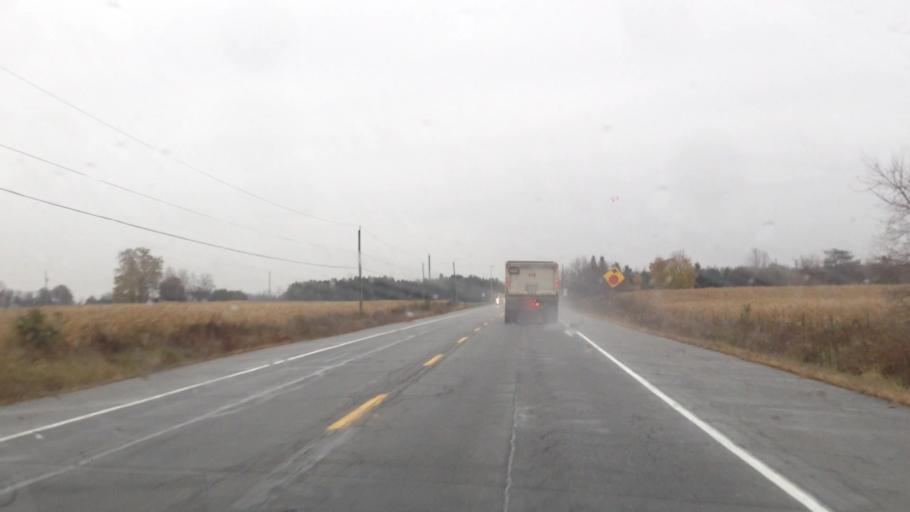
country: CA
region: Ontario
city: Clarence-Rockland
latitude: 45.3483
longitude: -75.3672
